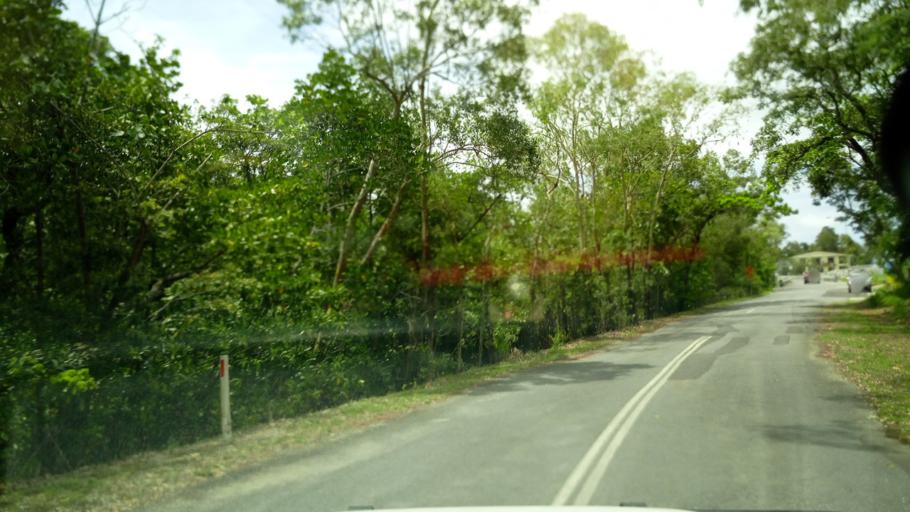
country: AU
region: Queensland
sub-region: Cairns
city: Redlynch
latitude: -16.8567
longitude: 145.7537
